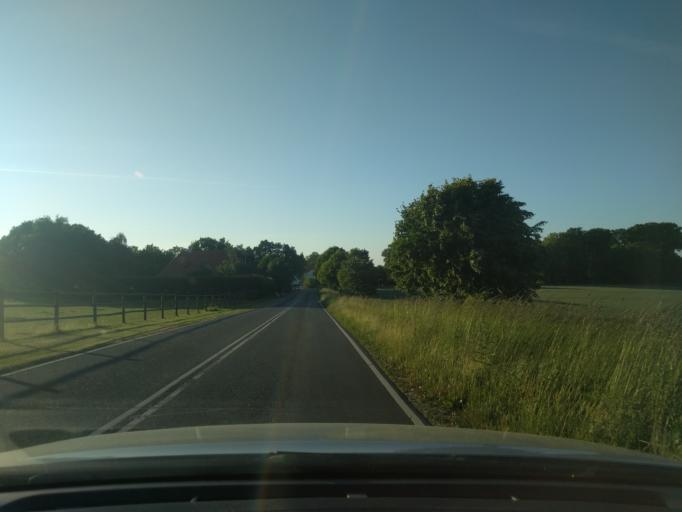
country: DK
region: South Denmark
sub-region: Kerteminde Kommune
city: Kerteminde
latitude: 55.5326
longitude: 10.6488
